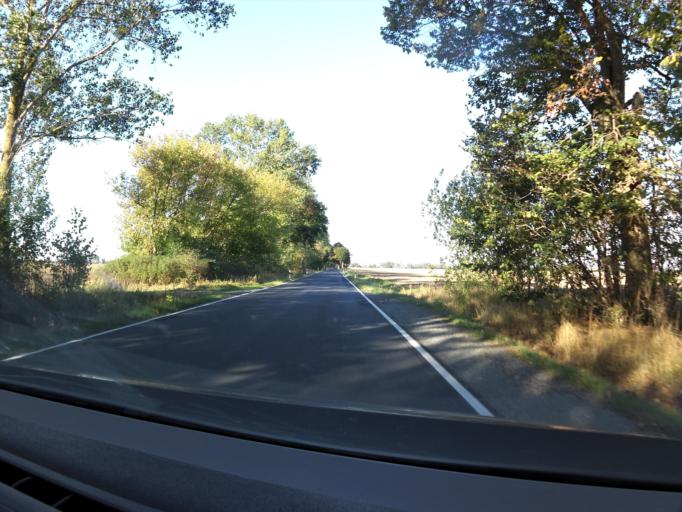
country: DE
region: Mecklenburg-Vorpommern
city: Alt-Sanitz
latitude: 53.8215
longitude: 13.5053
